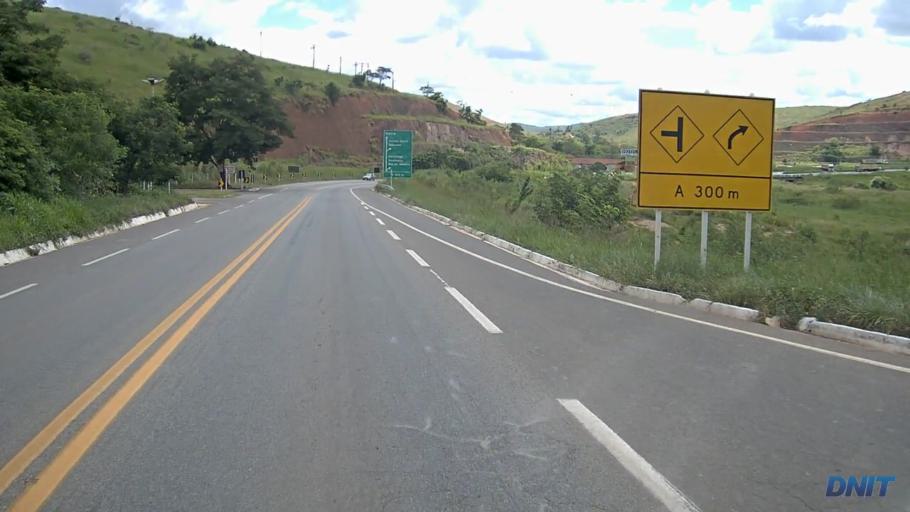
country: BR
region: Minas Gerais
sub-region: Governador Valadares
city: Governador Valadares
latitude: -18.8625
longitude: -41.9870
